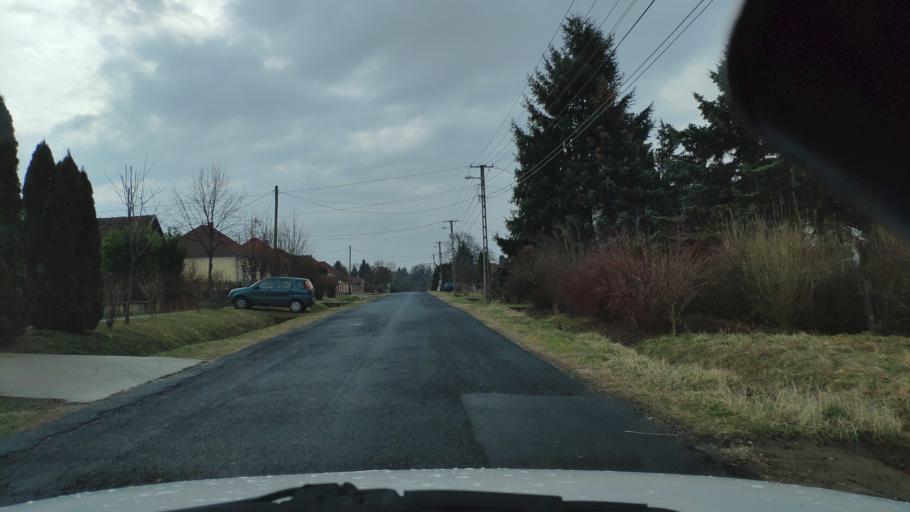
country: HU
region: Zala
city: Nagykanizsa
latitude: 46.4140
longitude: 16.9982
